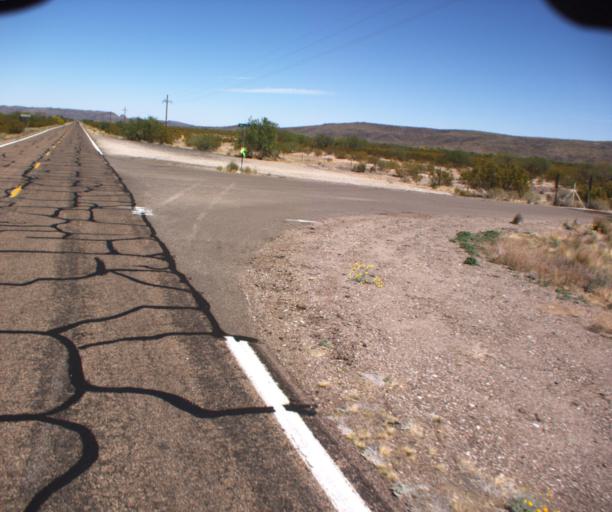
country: US
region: Arizona
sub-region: Pima County
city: Ajo
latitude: 32.4652
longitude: -112.8744
